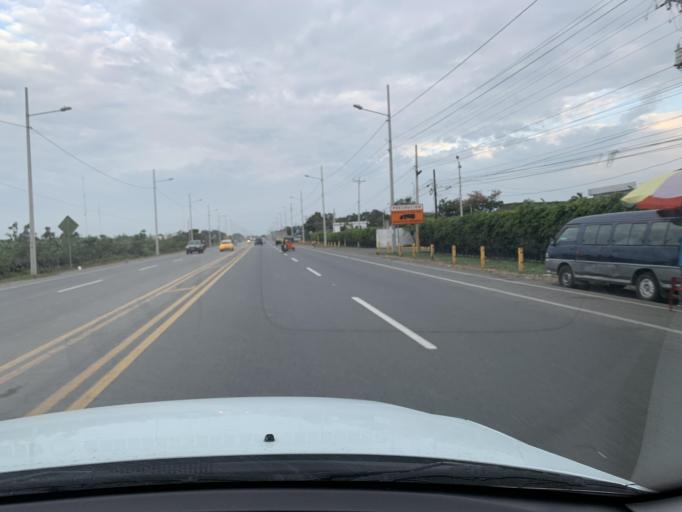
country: EC
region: Guayas
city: Yaguachi Nuevo
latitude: -2.2523
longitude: -79.6344
